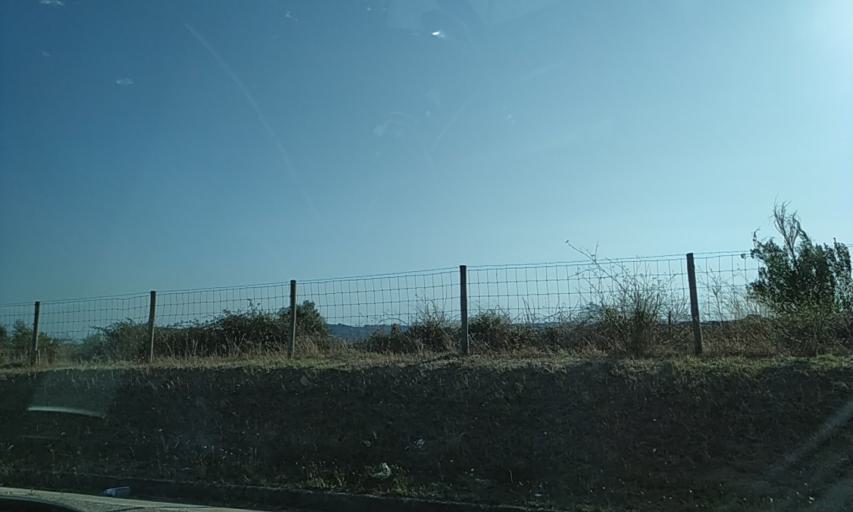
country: PT
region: Santarem
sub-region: Santarem
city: Santarem
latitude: 39.2282
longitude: -8.7043
